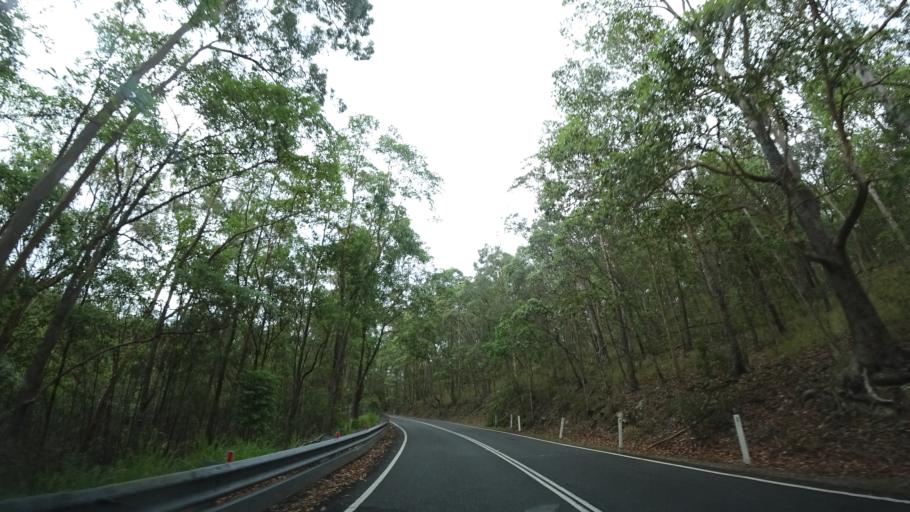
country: AU
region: Queensland
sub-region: Brisbane
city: Taringa
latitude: -27.4632
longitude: 152.9559
